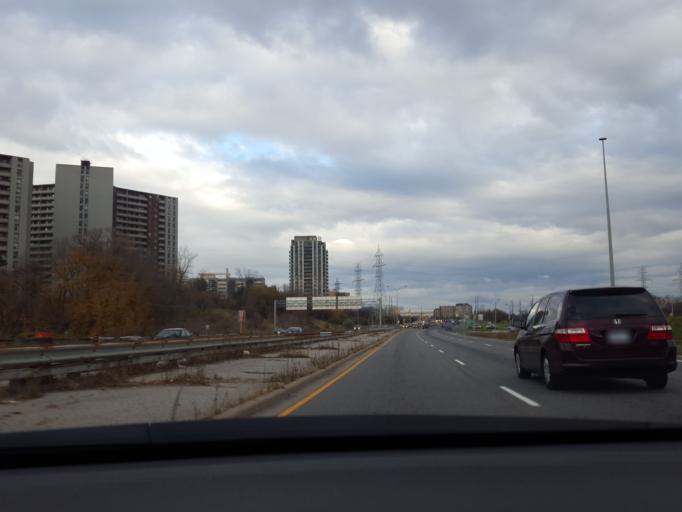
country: CA
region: Ontario
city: Etobicoke
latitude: 43.6736
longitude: -79.5711
